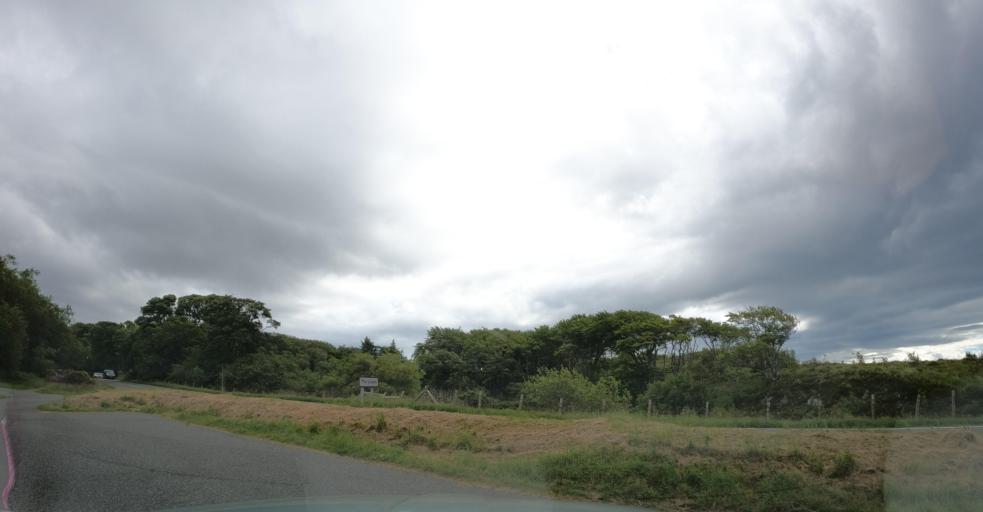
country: GB
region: Scotland
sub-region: Eilean Siar
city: Stornoway
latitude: 58.2049
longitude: -6.4204
